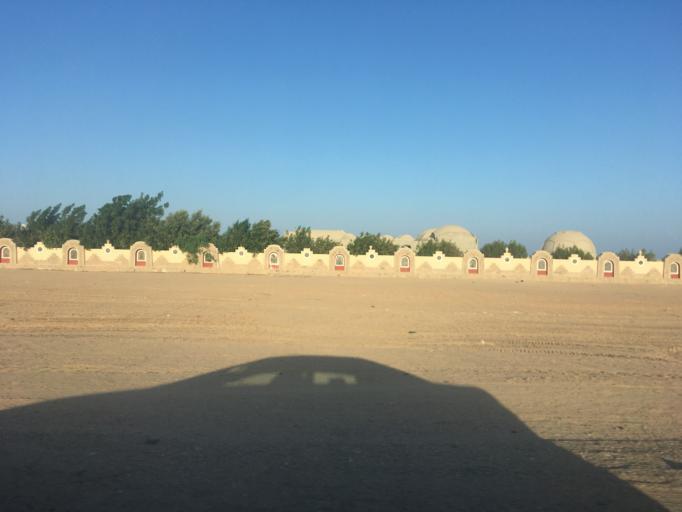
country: EG
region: Red Sea
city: Marsa Alam
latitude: 24.9053
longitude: 34.9670
